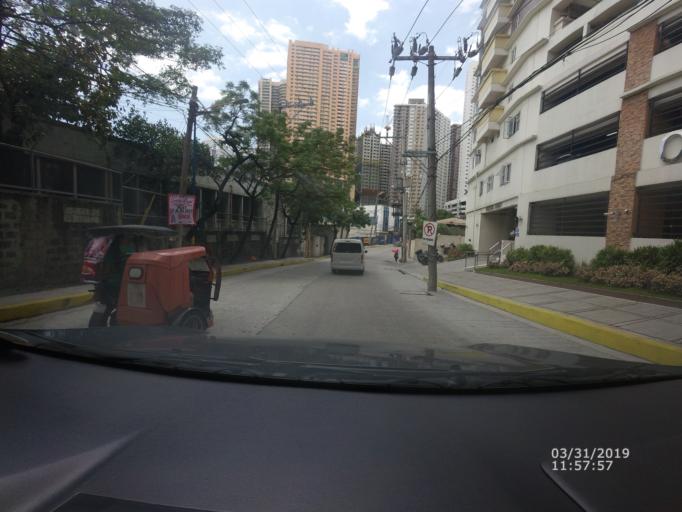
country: PH
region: Metro Manila
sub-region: Mandaluyong
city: Mandaluyong City
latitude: 14.5741
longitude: 121.0509
